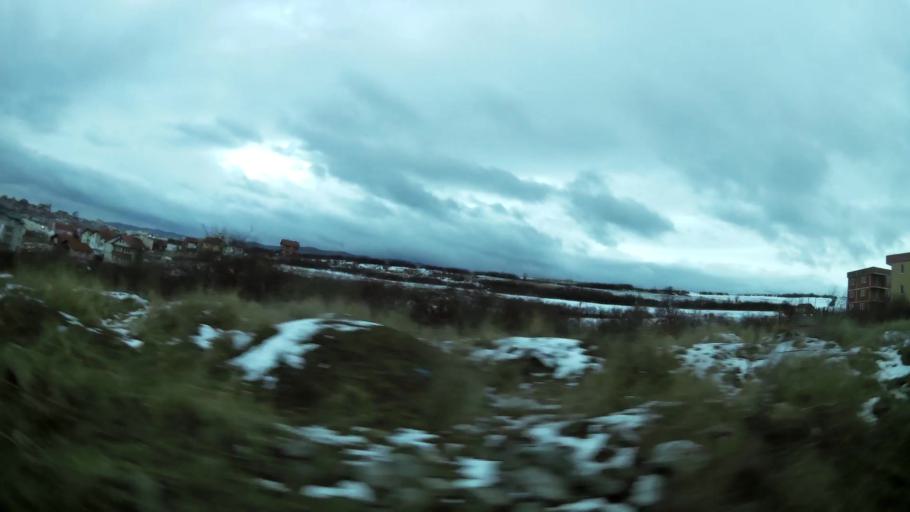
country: XK
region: Pristina
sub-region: Komuna e Prishtines
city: Pristina
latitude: 42.6376
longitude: 21.1648
